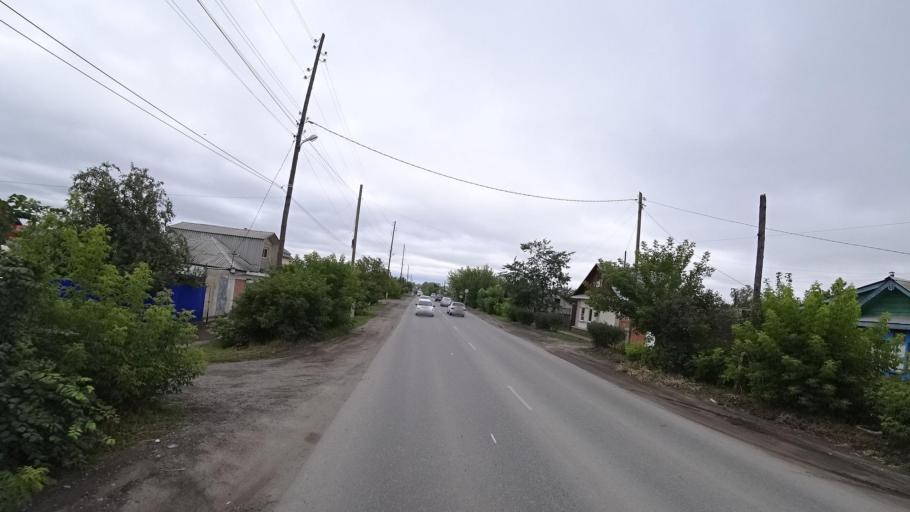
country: RU
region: Sverdlovsk
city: Kamyshlov
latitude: 56.8401
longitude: 62.7279
